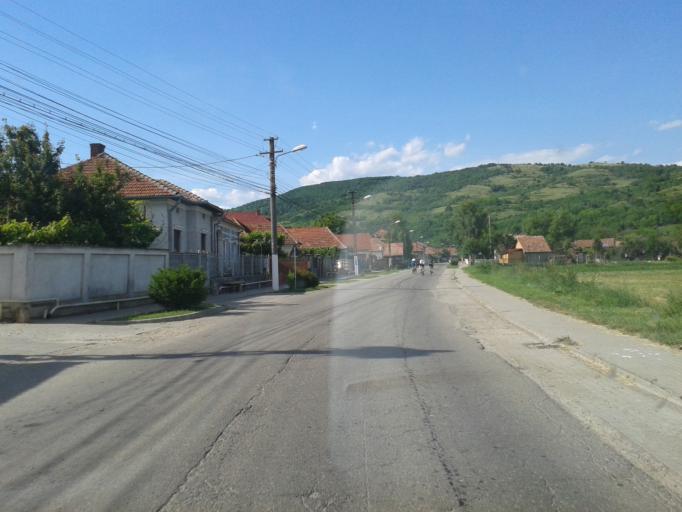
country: RO
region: Hunedoara
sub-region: Comuna Geoagiu
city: Geoagiu
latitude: 45.9267
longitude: 23.1960
